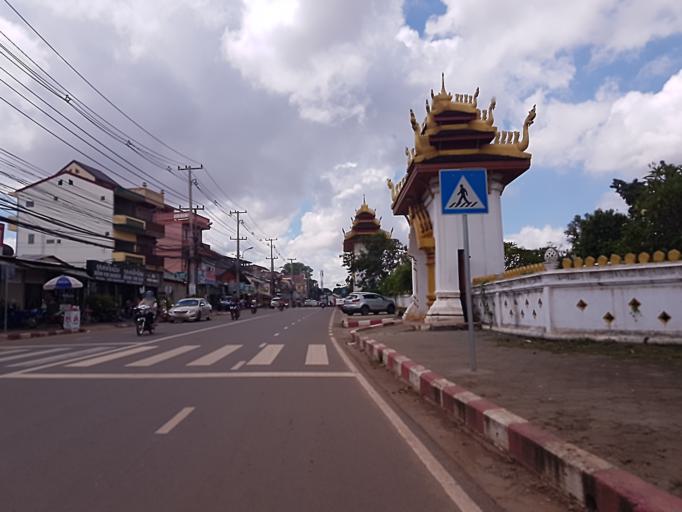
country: LA
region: Vientiane
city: Vientiane
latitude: 17.9751
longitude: 102.6368
